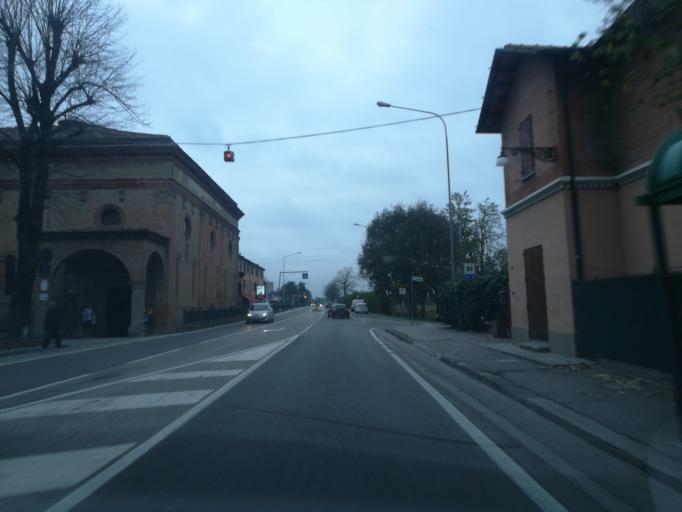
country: IT
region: Emilia-Romagna
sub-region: Provincia di Bologna
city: Toscanella
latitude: 44.3705
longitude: 11.6705
